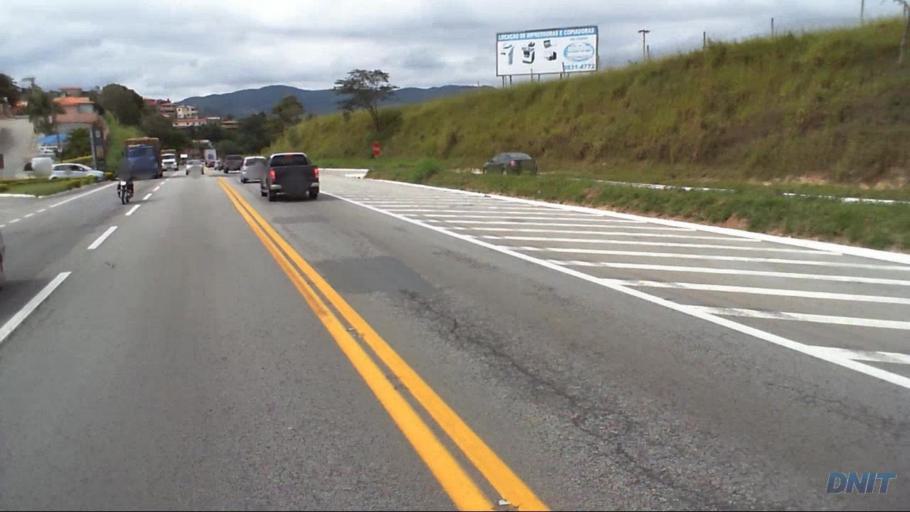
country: BR
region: Minas Gerais
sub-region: Caete
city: Caete
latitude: -19.7244
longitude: -43.5843
